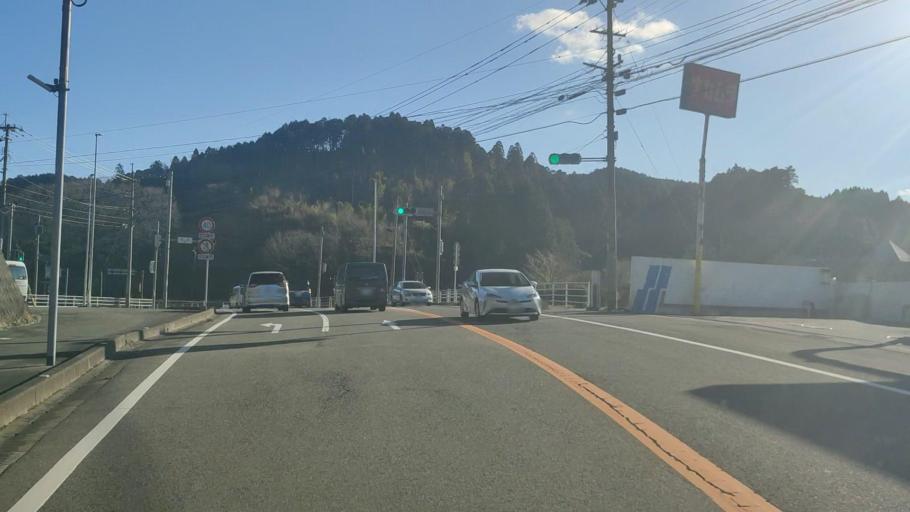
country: JP
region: Saga Prefecture
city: Kanzakimachi-kanzaki
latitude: 33.4228
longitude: 130.2773
